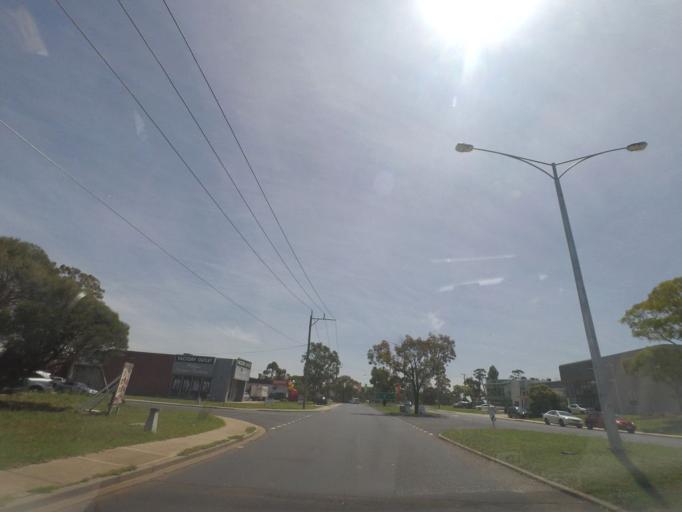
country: AU
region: Victoria
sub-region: Brimbank
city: Keilor Park
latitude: -37.7136
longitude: 144.8610
